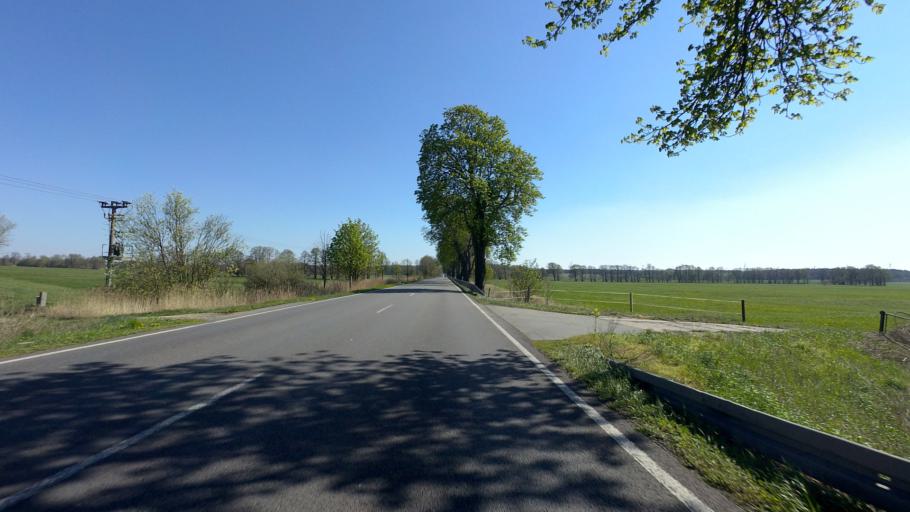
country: DE
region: Saxony-Anhalt
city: Klotze
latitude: 52.6972
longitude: 11.2589
